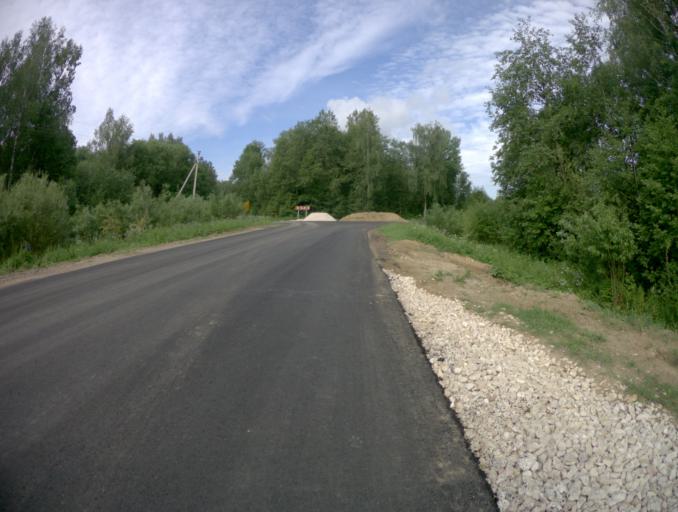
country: RU
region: Vladimir
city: Lakinsk
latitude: 56.0701
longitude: 39.8858
